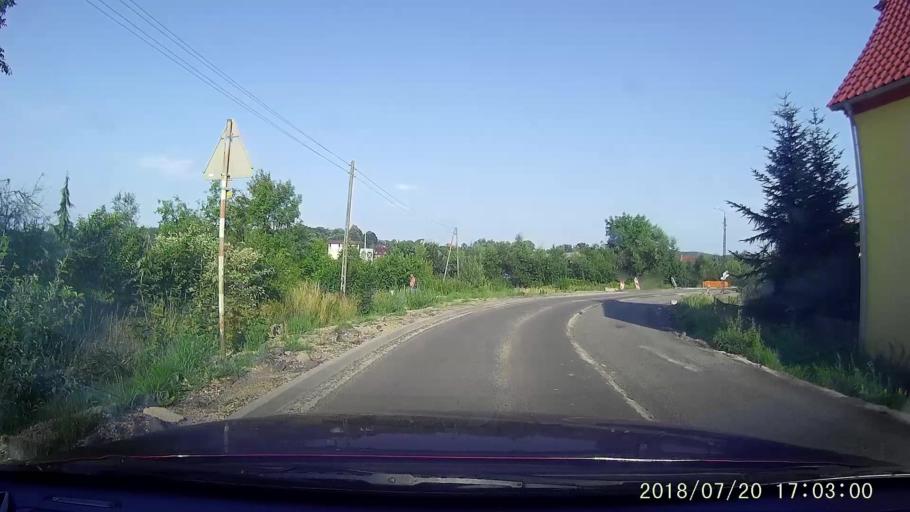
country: PL
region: Lower Silesian Voivodeship
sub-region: Powiat lubanski
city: Lesna
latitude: 51.0293
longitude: 15.2582
